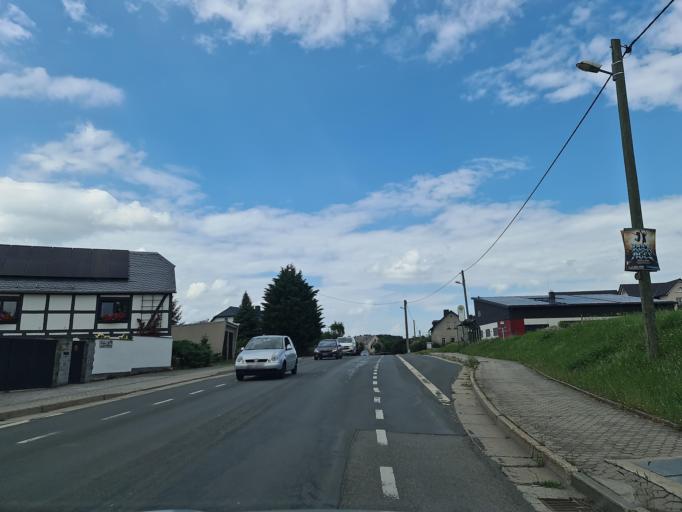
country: DE
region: Saxony
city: Pohl
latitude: 50.5296
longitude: 12.1781
